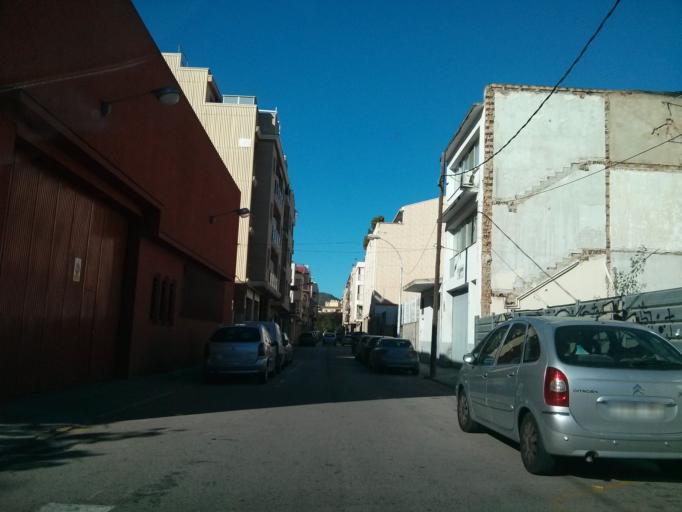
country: ES
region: Catalonia
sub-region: Provincia de Tarragona
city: El Vendrell
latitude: 41.2140
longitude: 1.5335
